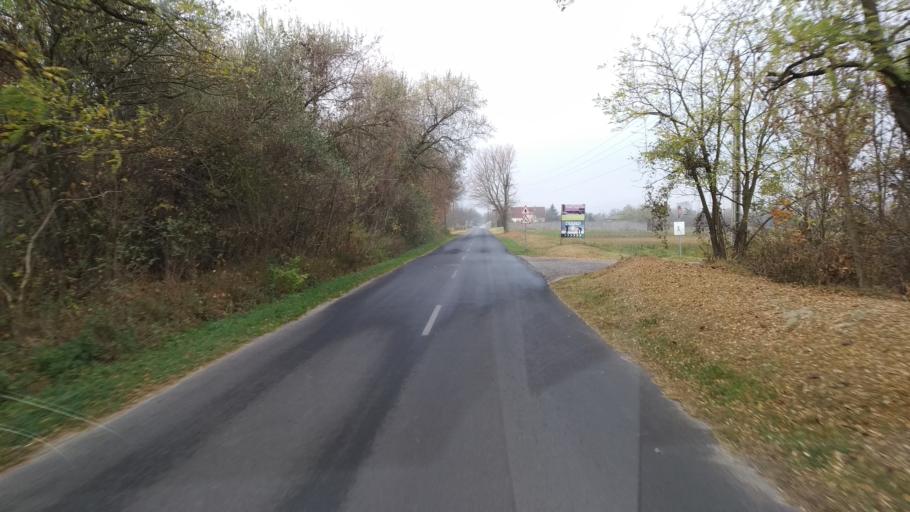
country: HU
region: Pest
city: Dunabogdany
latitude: 47.8041
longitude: 19.0249
